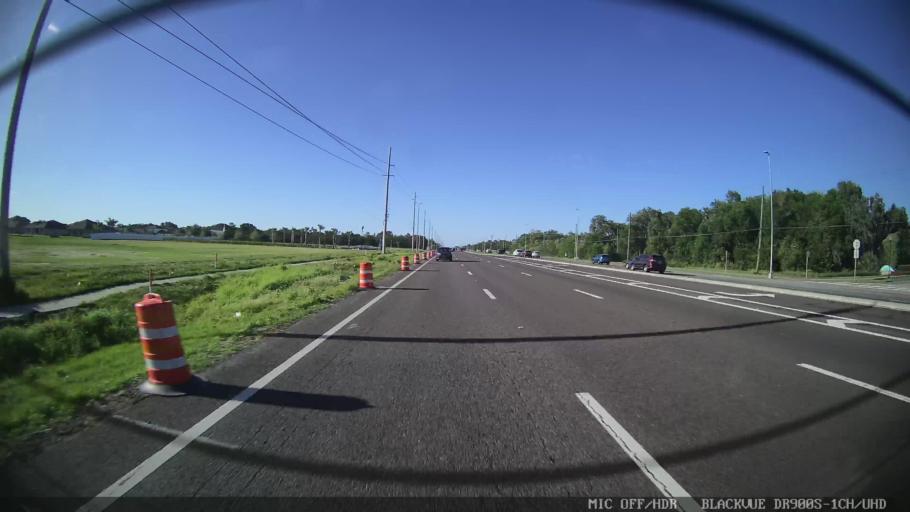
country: US
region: Florida
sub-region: Hillsborough County
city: Sun City Center
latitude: 27.7770
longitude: -82.3336
